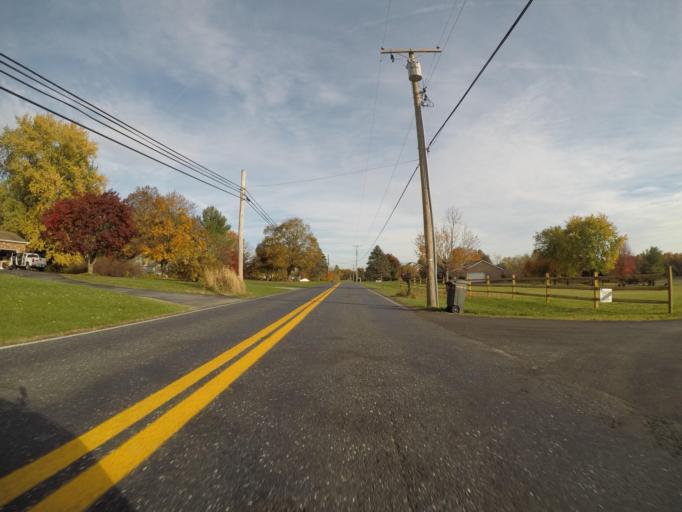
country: US
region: Maryland
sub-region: Carroll County
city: Westminster
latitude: 39.5874
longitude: -76.9231
